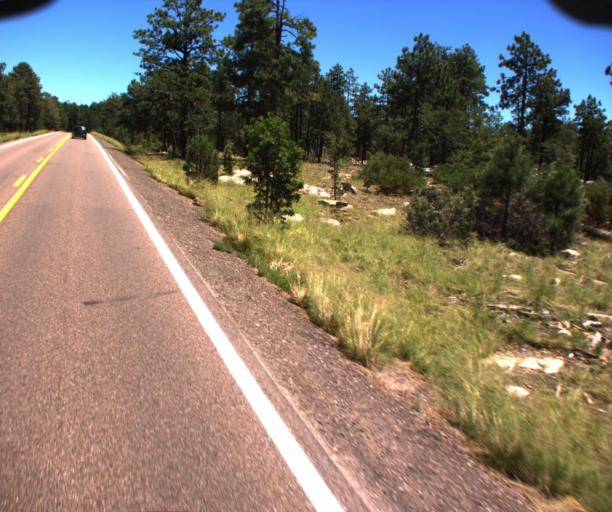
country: US
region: Arizona
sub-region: Gila County
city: Pine
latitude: 34.4389
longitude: -111.4958
